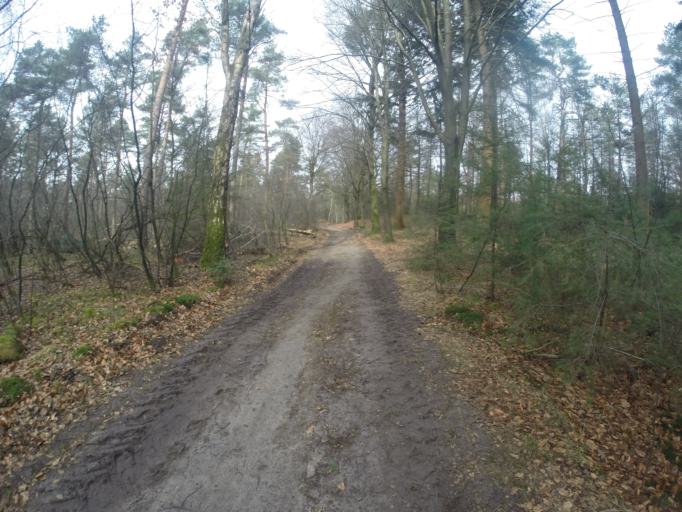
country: NL
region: Gelderland
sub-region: Gemeente Bronckhorst
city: Zelhem
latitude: 52.0372
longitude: 6.3836
